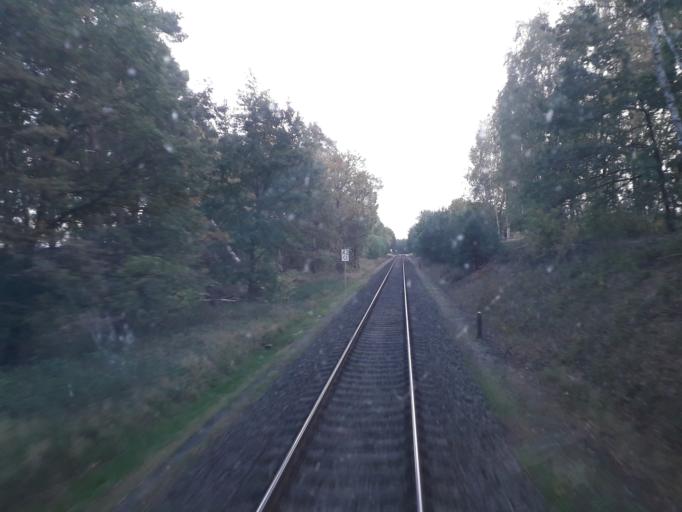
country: DE
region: Brandenburg
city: Walsleben
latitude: 52.9788
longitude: 12.6411
